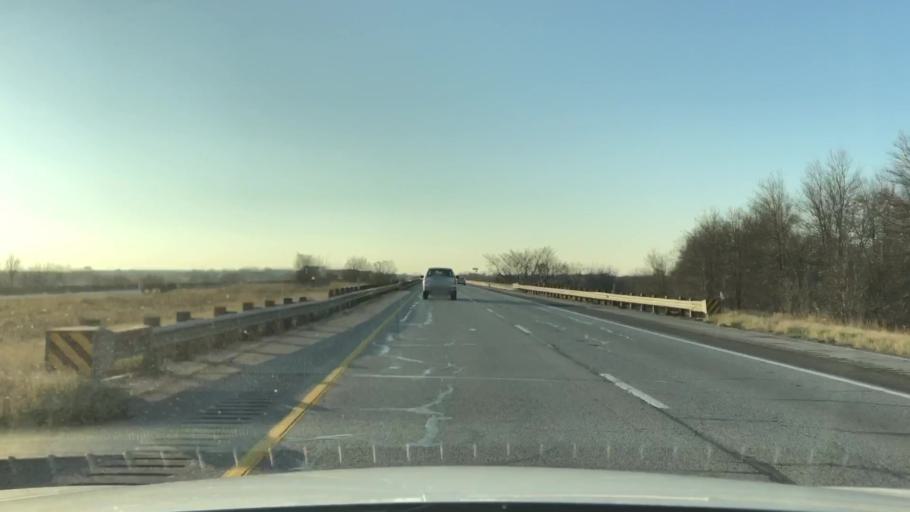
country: US
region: Texas
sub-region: Caldwell County
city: Luling
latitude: 29.6499
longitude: -97.6393
